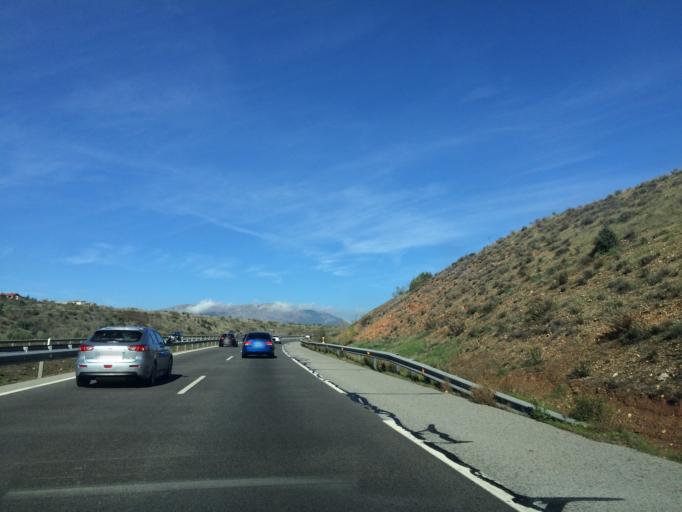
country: ES
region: Madrid
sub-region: Provincia de Madrid
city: Venturada
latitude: 40.8047
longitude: -3.6185
